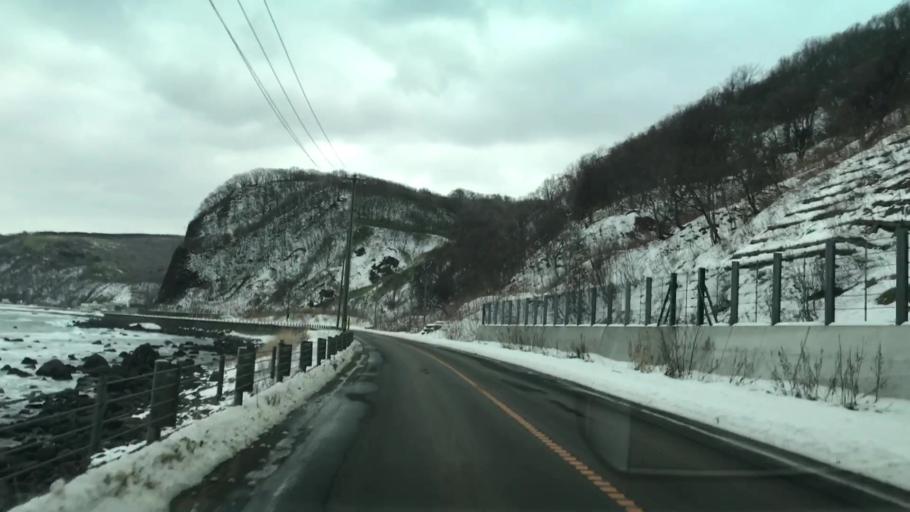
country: JP
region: Hokkaido
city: Iwanai
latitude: 43.3313
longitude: 140.4144
